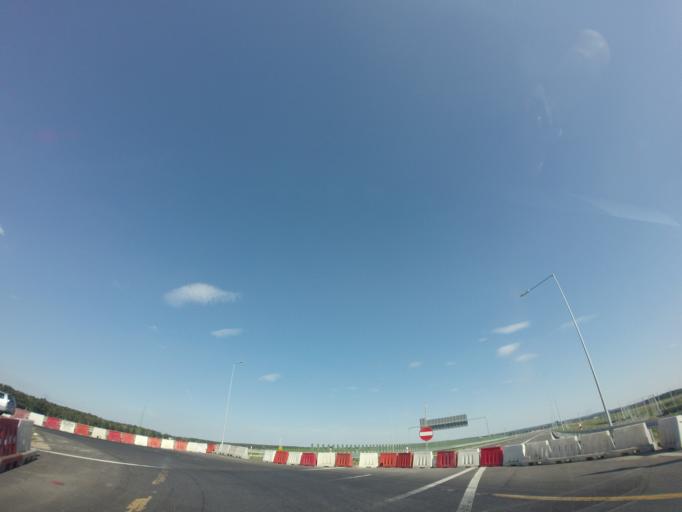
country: PL
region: Lubusz
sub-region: Powiat nowosolski
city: Nowe Miasteczko
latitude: 51.7276
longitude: 15.7318
